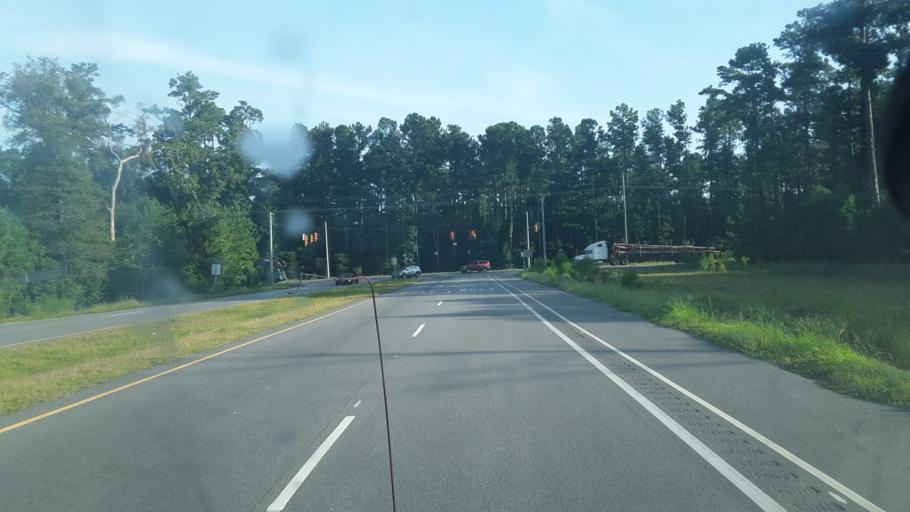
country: US
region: South Carolina
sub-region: Horry County
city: Red Hill
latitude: 33.8210
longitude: -78.9142
